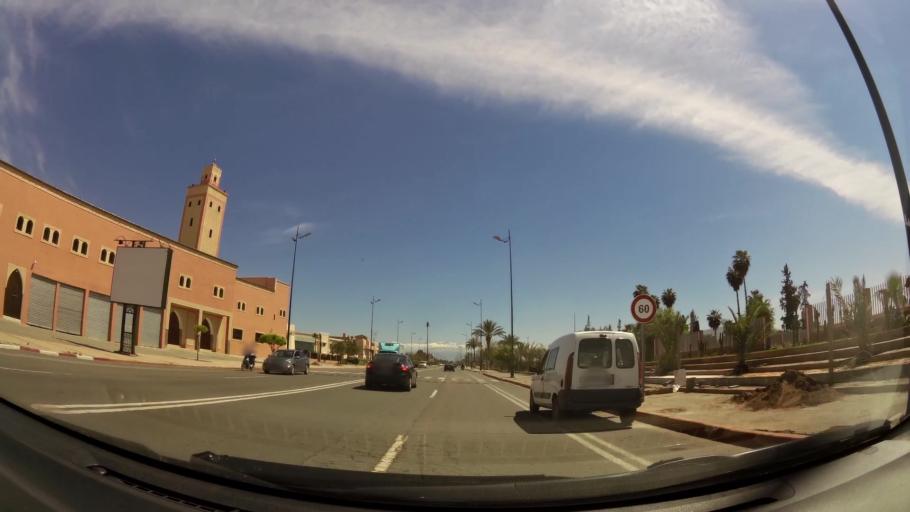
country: MA
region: Marrakech-Tensift-Al Haouz
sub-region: Marrakech
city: Marrakesh
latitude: 31.6128
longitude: -7.9748
